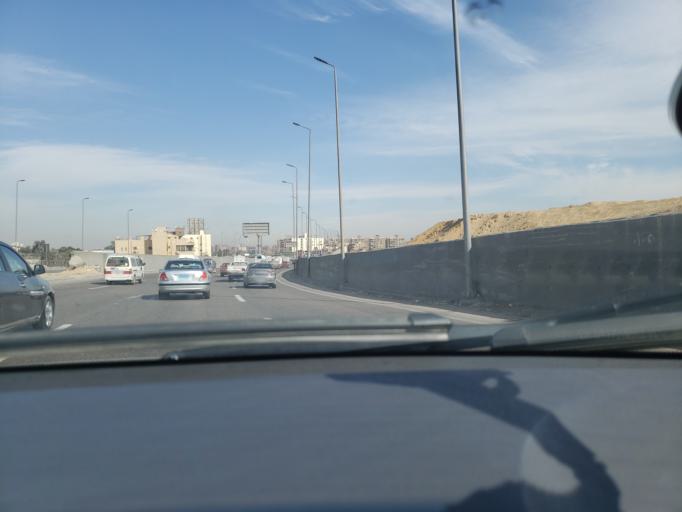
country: EG
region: Al Jizah
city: Al Jizah
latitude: 29.9967
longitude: 31.1129
